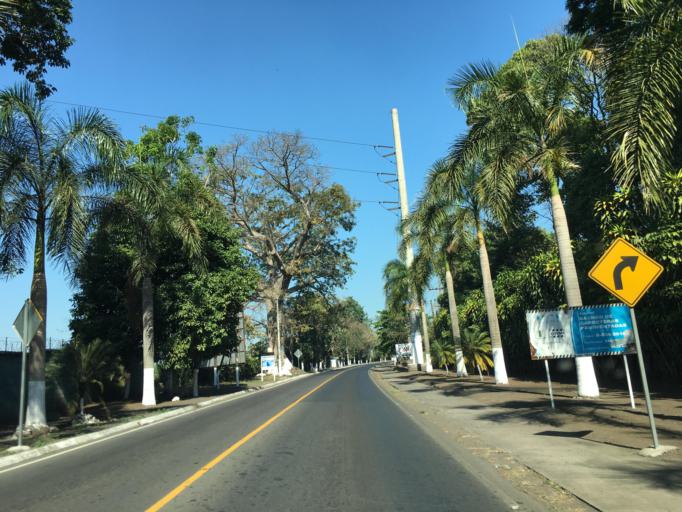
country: GT
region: Escuintla
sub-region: Municipio de La Democracia
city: La Democracia
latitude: 14.2351
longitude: -90.9515
